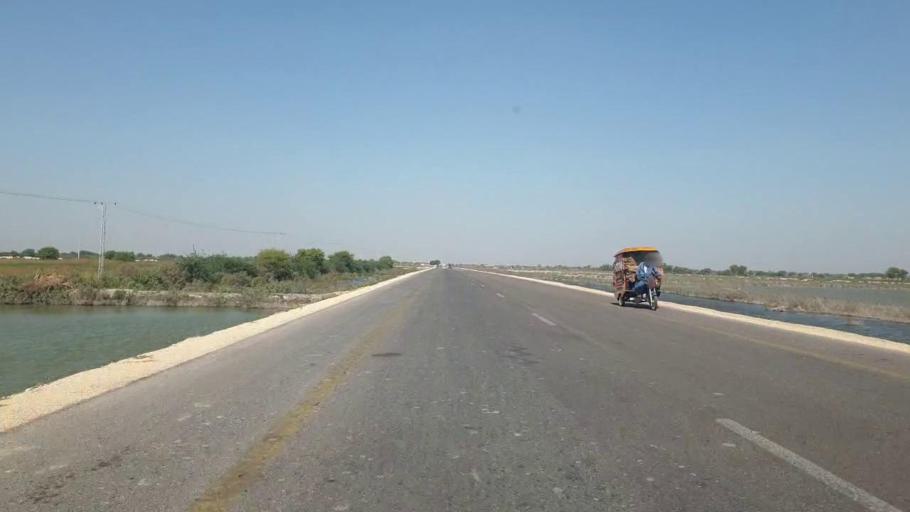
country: PK
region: Sindh
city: Talhar
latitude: 24.8402
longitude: 68.8162
